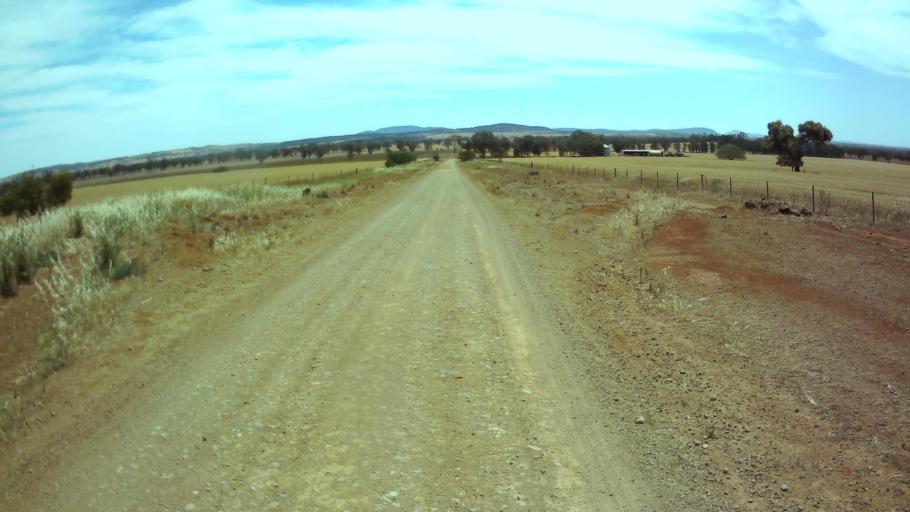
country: AU
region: New South Wales
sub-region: Weddin
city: Grenfell
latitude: -33.7496
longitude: 148.1518
